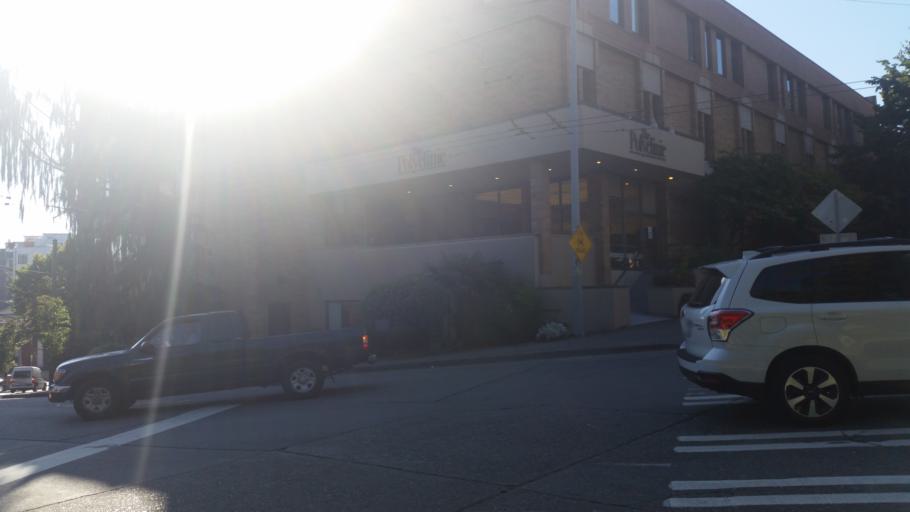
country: US
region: Washington
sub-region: King County
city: Seattle
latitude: 47.6129
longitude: -122.3222
